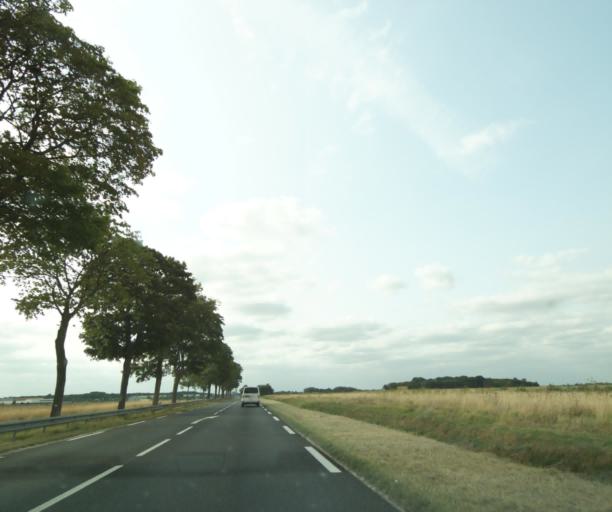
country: FR
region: Centre
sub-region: Departement d'Indre-et-Loire
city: Truyes
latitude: 47.2497
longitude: 0.8517
